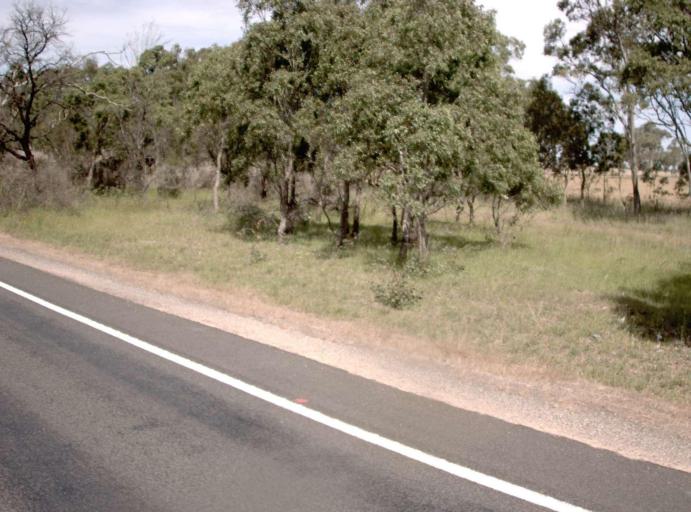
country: AU
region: Victoria
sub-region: East Gippsland
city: Bairnsdale
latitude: -37.8626
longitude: 147.5057
